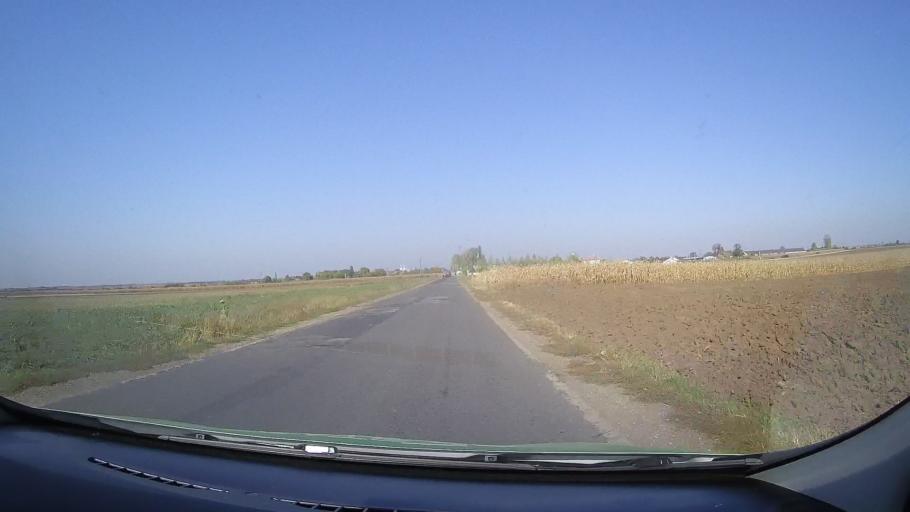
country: RO
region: Satu Mare
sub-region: Comuna Sanislau
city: Sanislau
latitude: 47.6262
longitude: 22.3389
